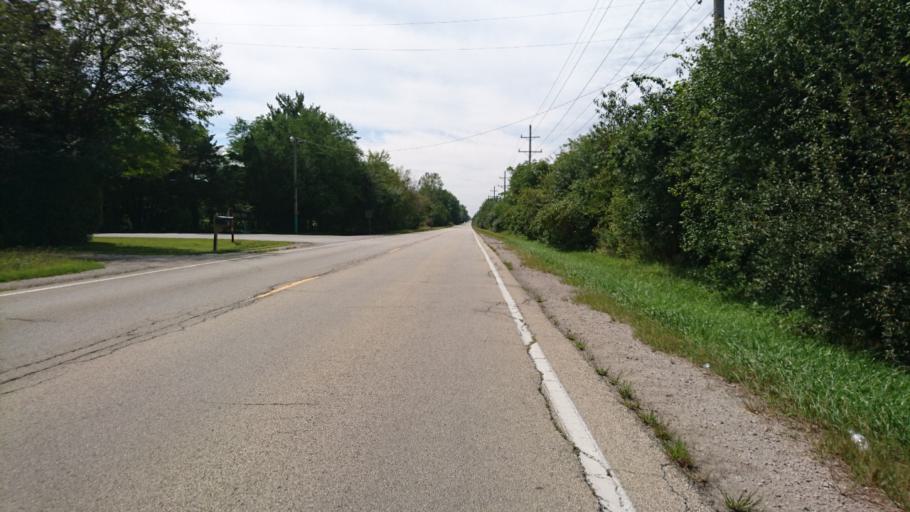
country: US
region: Illinois
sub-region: Will County
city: Braidwood
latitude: 41.2829
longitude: -88.1878
